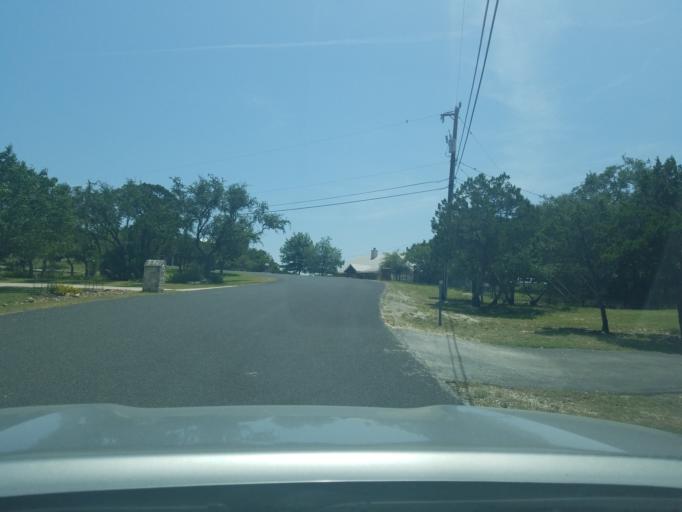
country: US
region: Texas
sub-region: Bexar County
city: Timberwood Park
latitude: 29.6685
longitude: -98.5130
